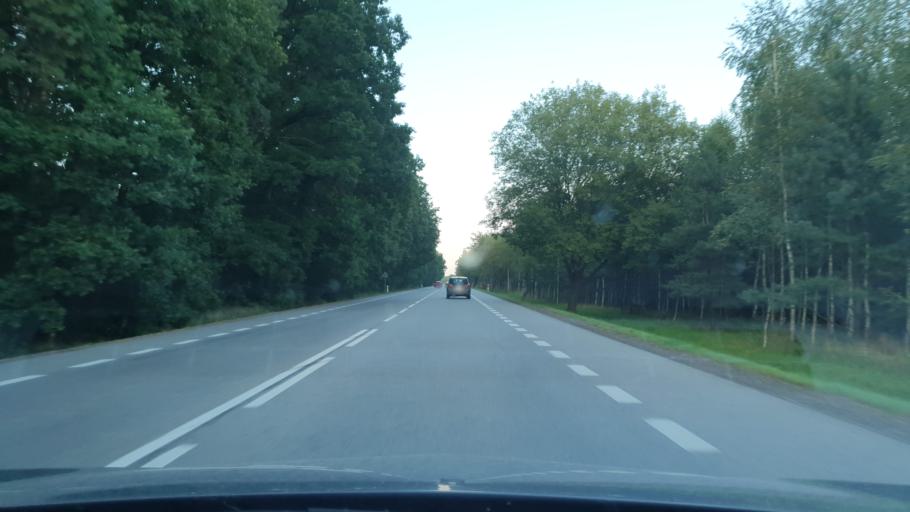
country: PL
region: Pomeranian Voivodeship
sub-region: Powiat leborski
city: Nowa Wies Leborska
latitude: 54.4947
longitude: 17.6155
